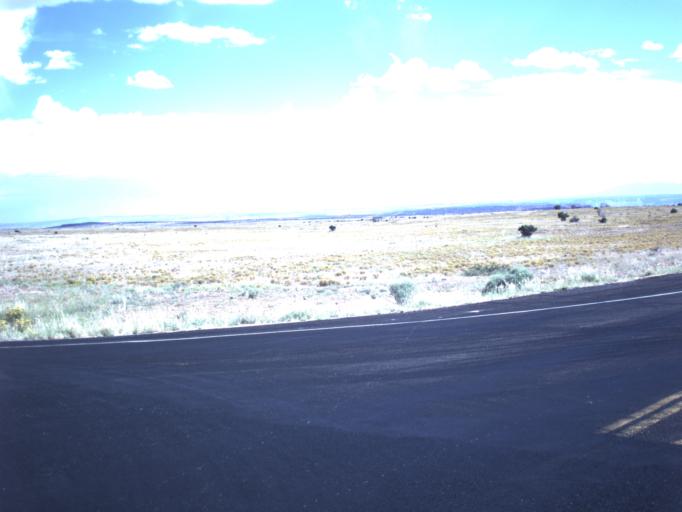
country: US
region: Utah
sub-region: Grand County
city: Moab
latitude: 38.5526
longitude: -109.7925
